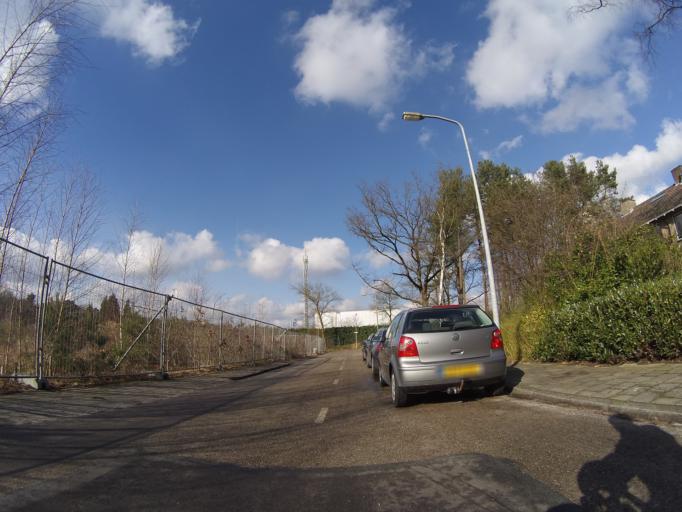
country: NL
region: Utrecht
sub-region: Gemeente Zeist
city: Zeist
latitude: 52.1371
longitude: 5.2331
